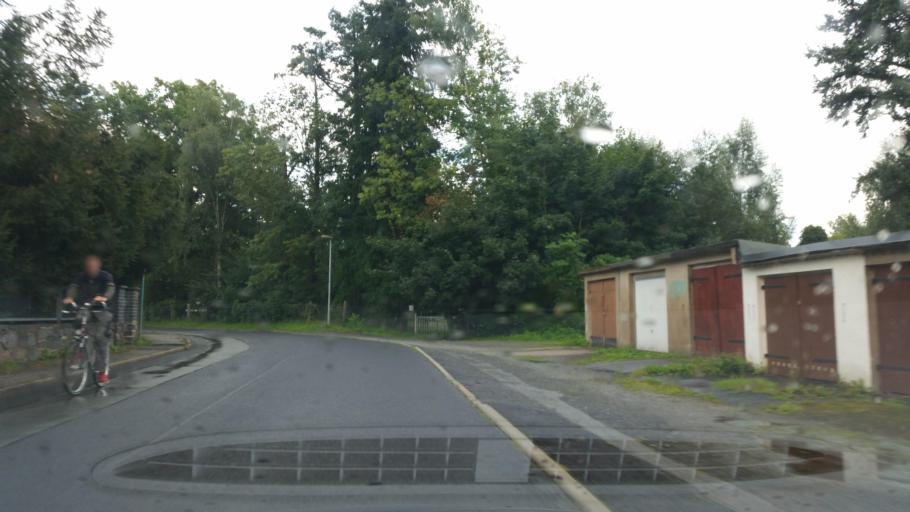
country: DE
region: Saxony
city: Lobau
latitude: 51.0920
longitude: 14.6720
